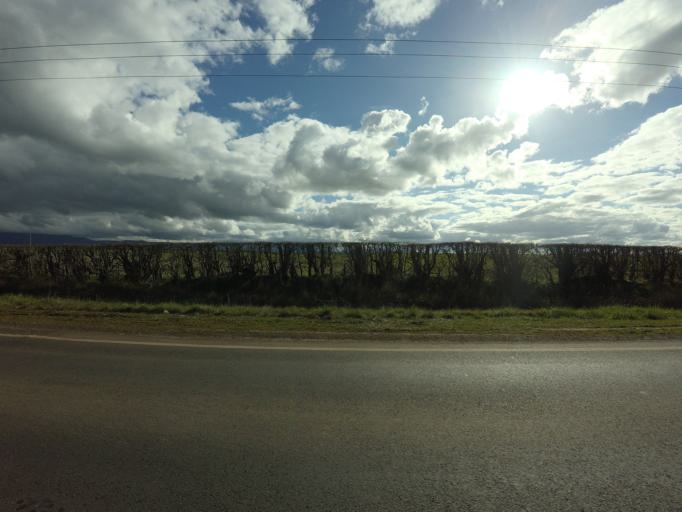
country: AU
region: Tasmania
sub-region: Northern Midlands
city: Longford
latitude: -41.7008
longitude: 147.0771
